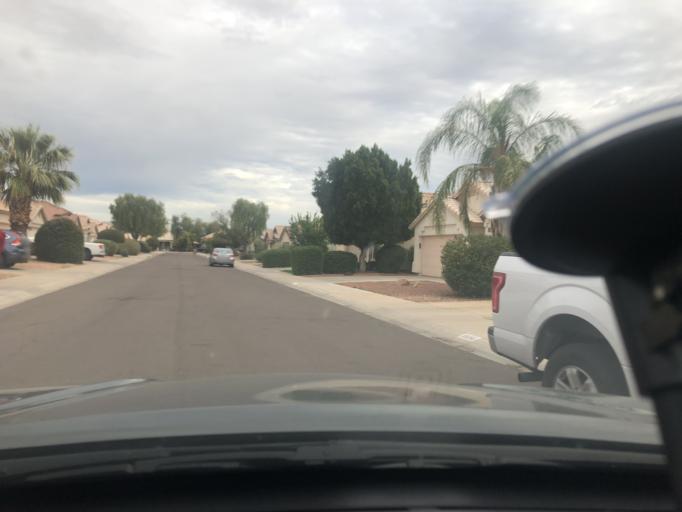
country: US
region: Arizona
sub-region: Maricopa County
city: Scottsdale
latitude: 33.4825
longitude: -111.8945
